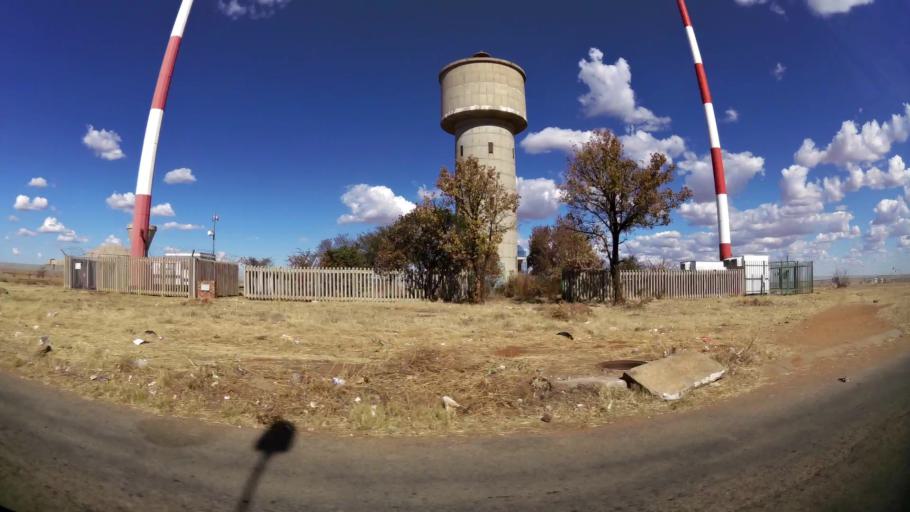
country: ZA
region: North-West
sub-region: Dr Kenneth Kaunda District Municipality
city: Klerksdorp
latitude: -26.8749
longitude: 26.5922
